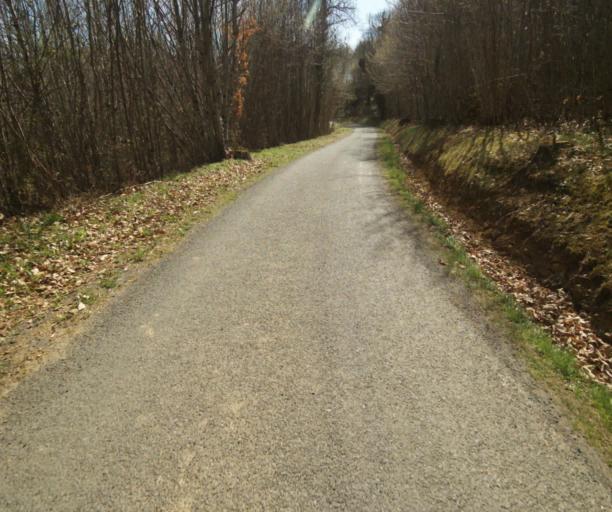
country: FR
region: Limousin
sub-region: Departement de la Correze
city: Seilhac
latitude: 45.3959
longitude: 1.7675
